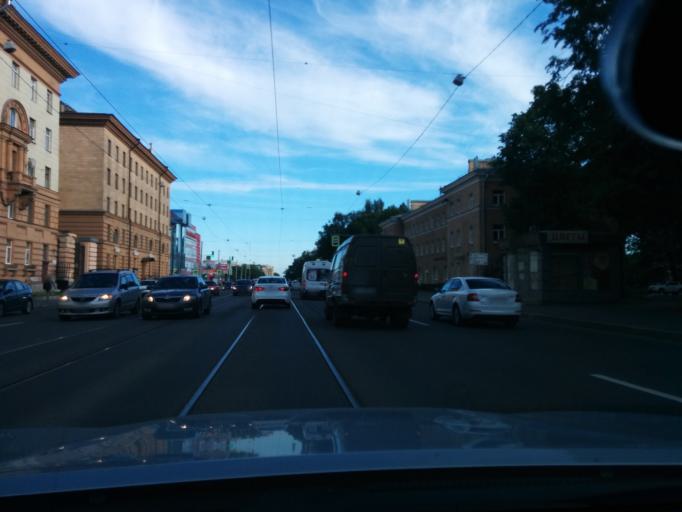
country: RU
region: Leningrad
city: Udel'naya
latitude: 60.0121
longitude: 30.3242
